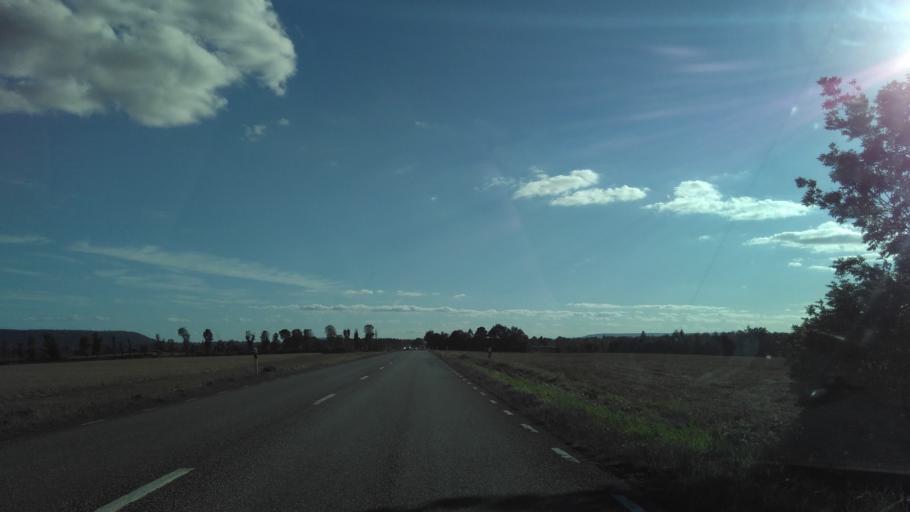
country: SE
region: Vaestra Goetaland
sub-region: Skovde Kommun
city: Skultorp
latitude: 58.2823
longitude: 13.7625
